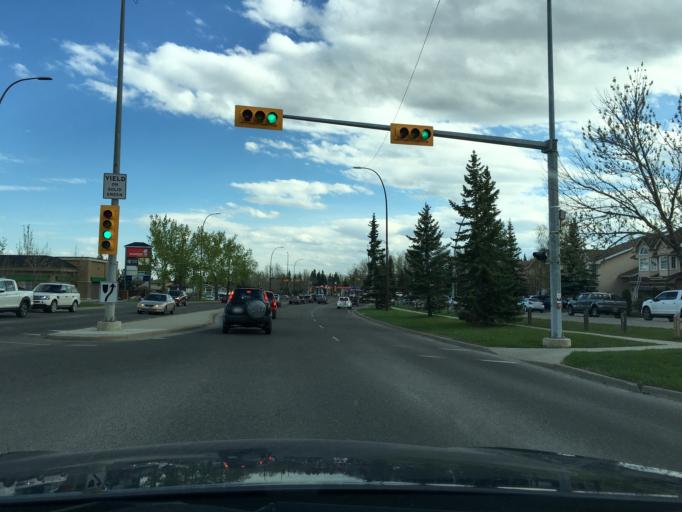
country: CA
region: Alberta
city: Calgary
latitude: 50.9145
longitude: -114.0739
